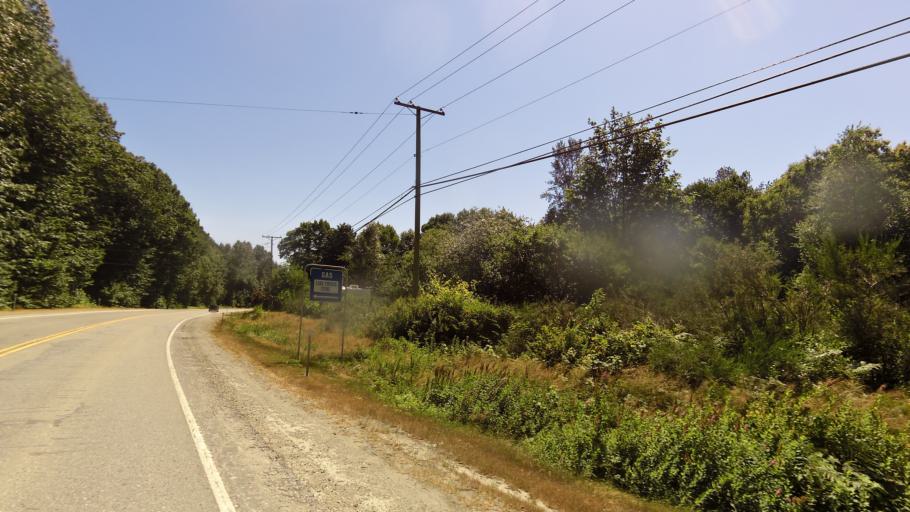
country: CA
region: British Columbia
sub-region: Fraser Valley Regional District
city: Chilliwack
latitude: 49.2229
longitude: -122.0125
